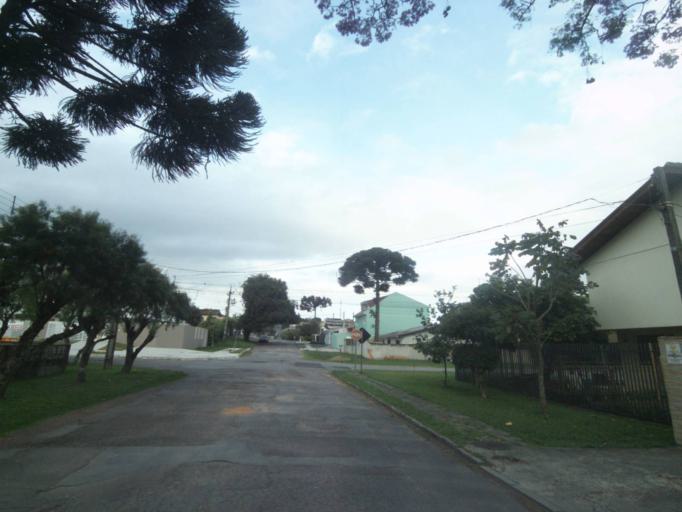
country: BR
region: Parana
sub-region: Pinhais
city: Pinhais
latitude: -25.4170
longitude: -49.2162
